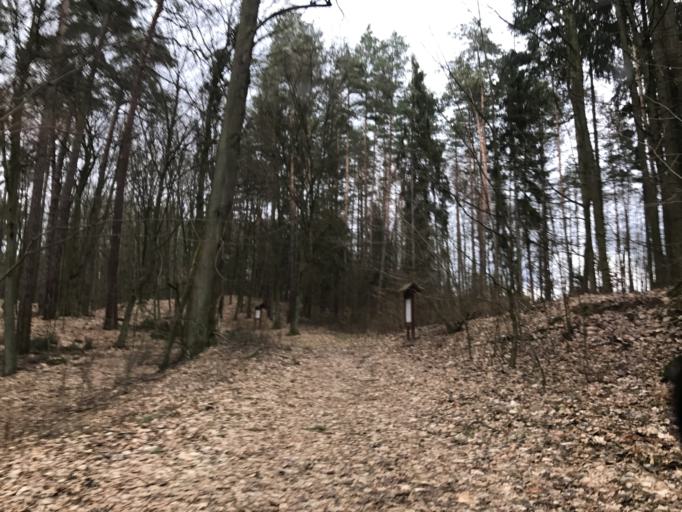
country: PL
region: Kujawsko-Pomorskie
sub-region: Powiat brodnicki
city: Gorzno
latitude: 53.1839
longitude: 19.6596
